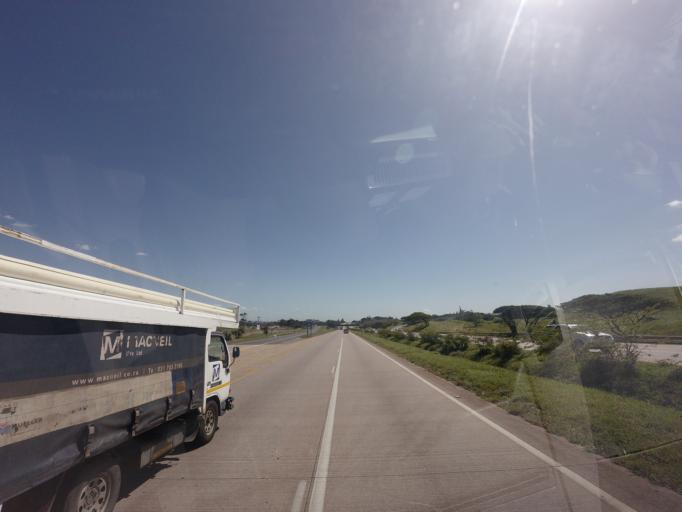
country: ZA
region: KwaZulu-Natal
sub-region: iLembe District Municipality
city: Ballitoville
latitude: -29.5061
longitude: 31.2077
